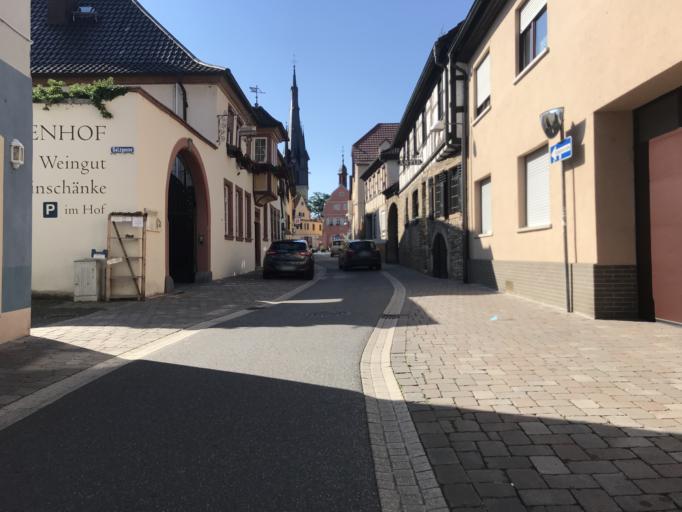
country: DE
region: Rheinland-Pfalz
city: Gau-Algesheim
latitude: 49.9578
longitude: 8.0151
